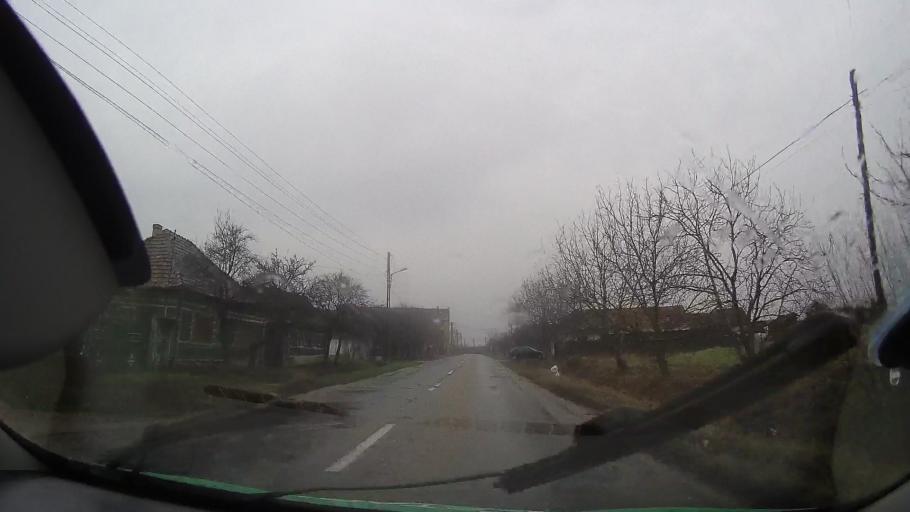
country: RO
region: Bihor
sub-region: Comuna Tulca
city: Tulca
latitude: 46.7859
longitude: 21.7882
